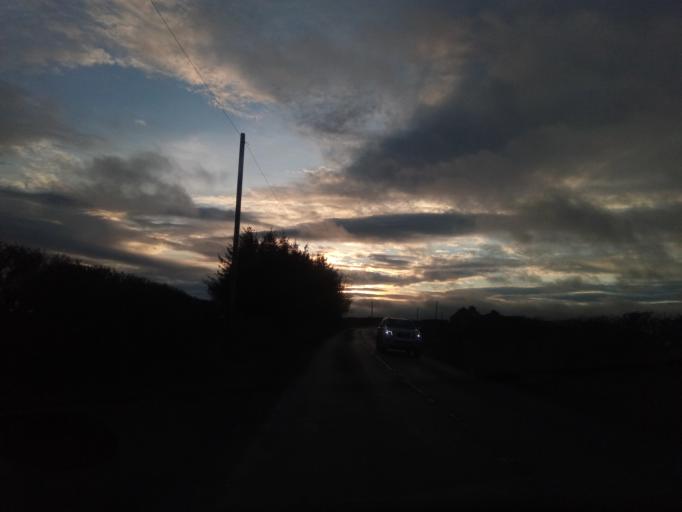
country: GB
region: England
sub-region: Northumberland
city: Meldon
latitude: 55.1373
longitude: -1.7572
